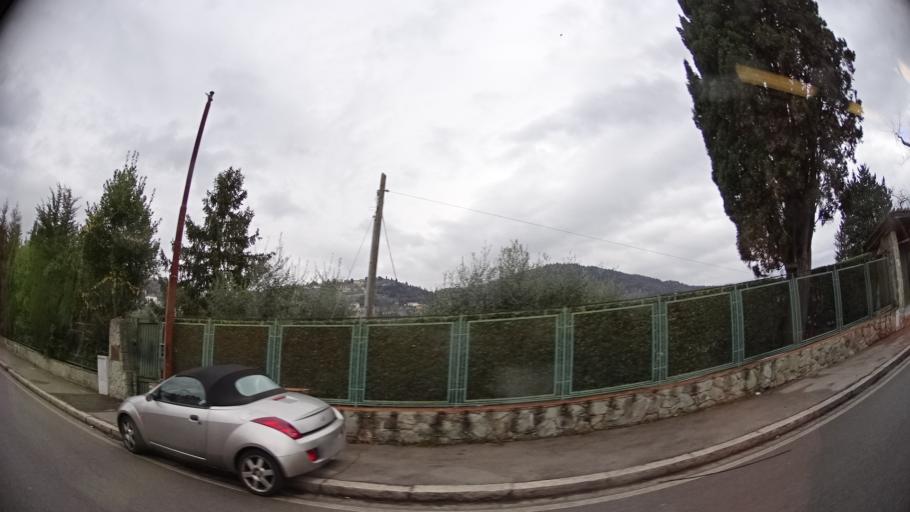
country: IT
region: Tuscany
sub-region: Province of Florence
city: Fiesole
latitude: 43.7975
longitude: 11.2849
